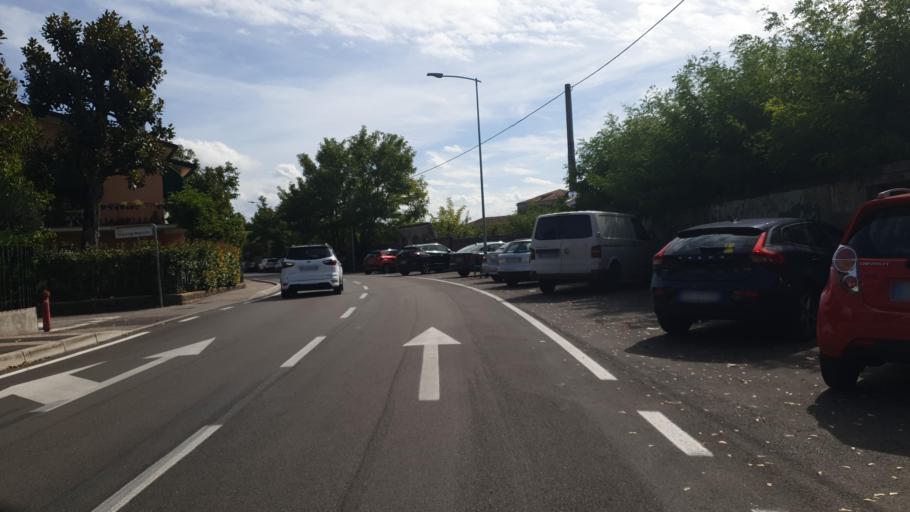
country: IT
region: Veneto
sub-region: Provincia di Padova
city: Piove di Sacco-Piovega
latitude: 45.2909
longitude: 12.0296
